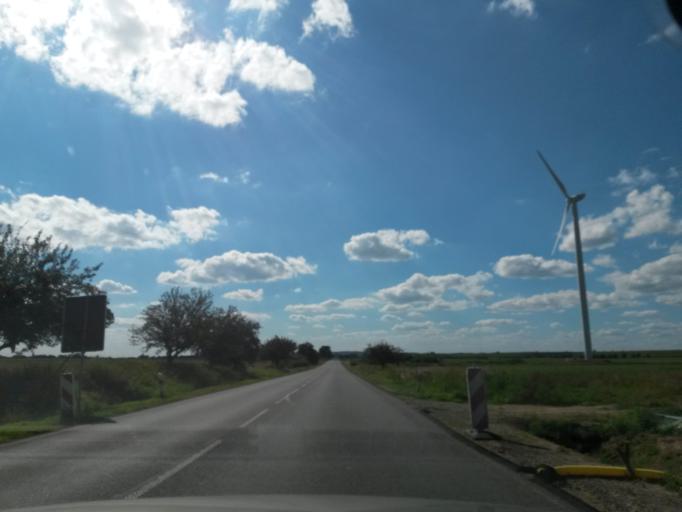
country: DE
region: Brandenburg
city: Pinnow
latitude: 53.0298
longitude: 14.0789
